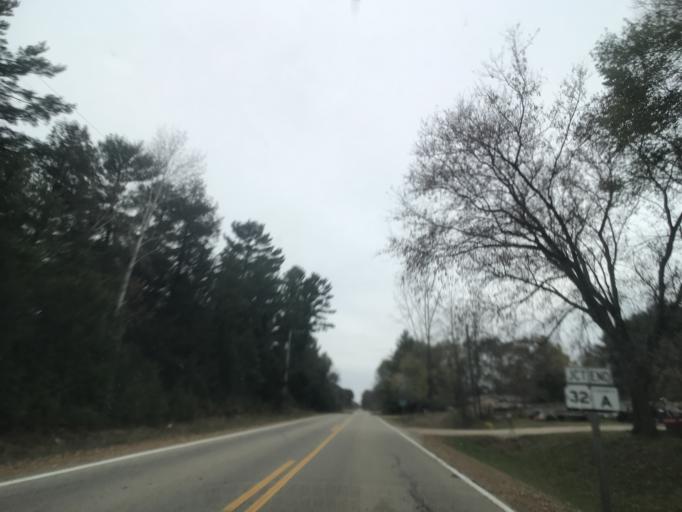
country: US
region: Wisconsin
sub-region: Oconto County
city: Gillett
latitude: 44.9838
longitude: -88.3225
